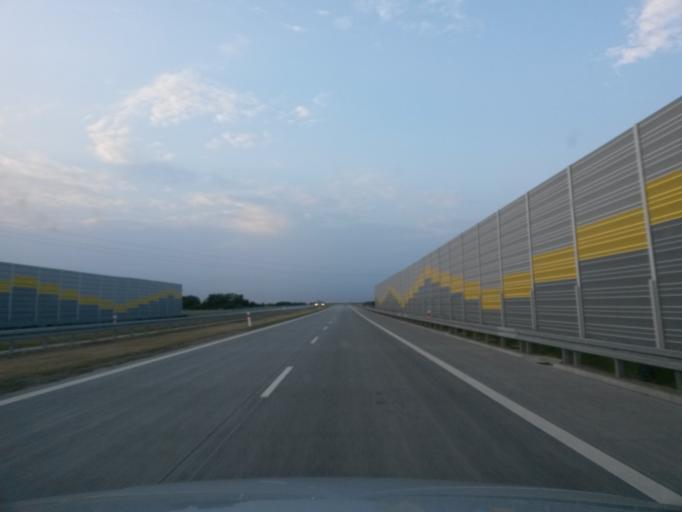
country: PL
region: Lodz Voivodeship
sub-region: Powiat sieradzki
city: Brzeznio
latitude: 51.4751
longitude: 18.6686
